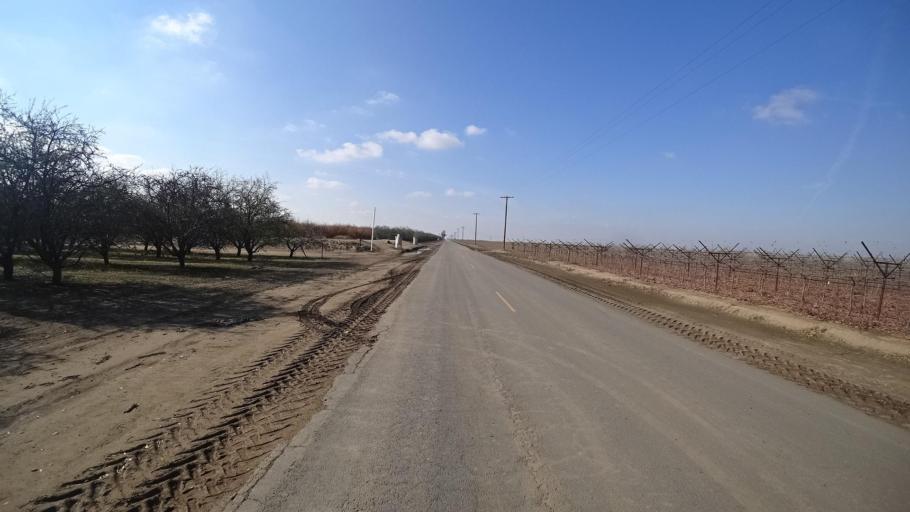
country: US
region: California
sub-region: Kern County
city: Arvin
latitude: 35.2384
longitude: -118.7966
